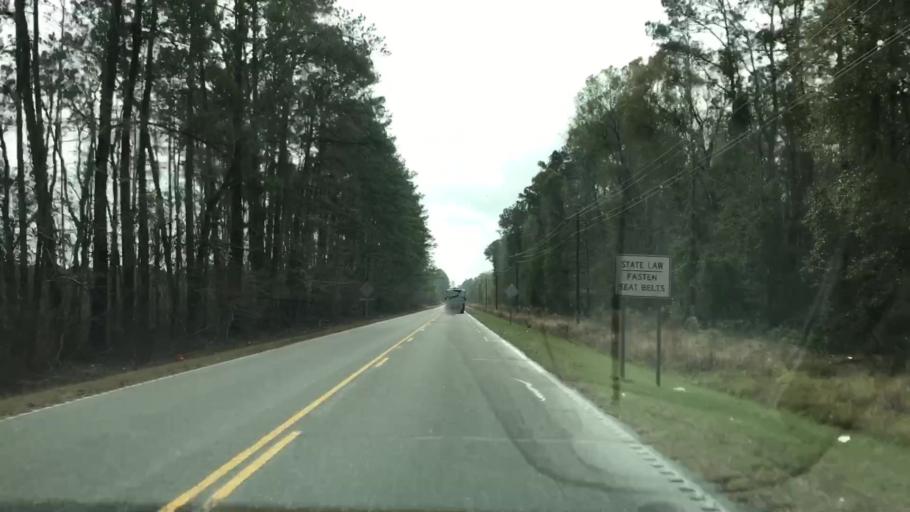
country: US
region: South Carolina
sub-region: Georgetown County
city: Murrells Inlet
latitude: 33.6303
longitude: -79.1887
